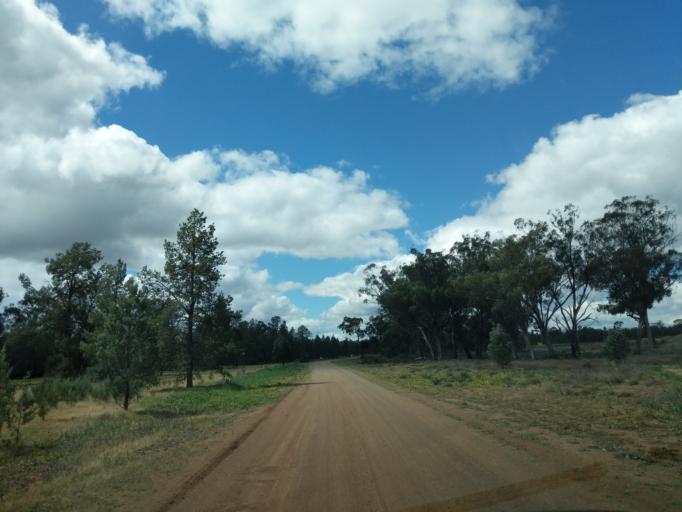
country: AU
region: New South Wales
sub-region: Coolamon
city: Coolamon
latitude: -34.8552
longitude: 146.9115
